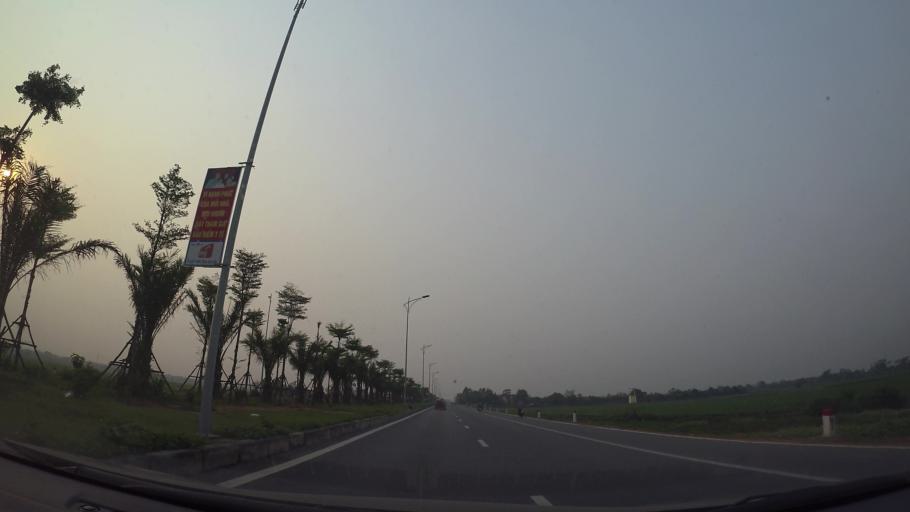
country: VN
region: Ha Noi
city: Kim Bai
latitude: 20.8804
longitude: 105.7995
